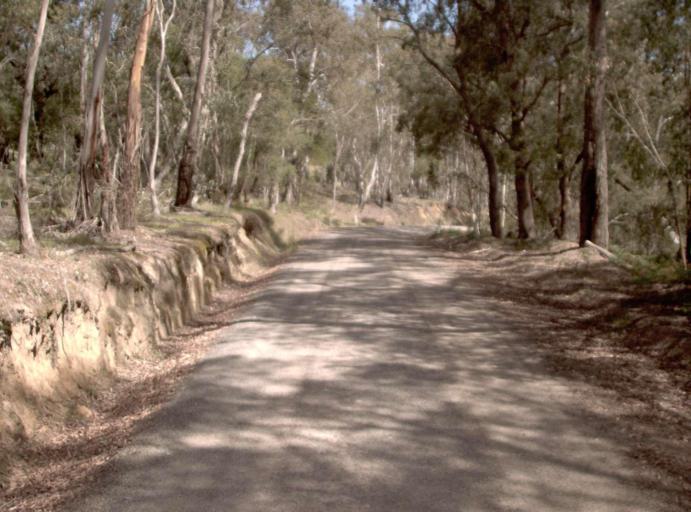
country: AU
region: New South Wales
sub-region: Bombala
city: Bombala
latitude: -37.1591
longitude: 148.6756
